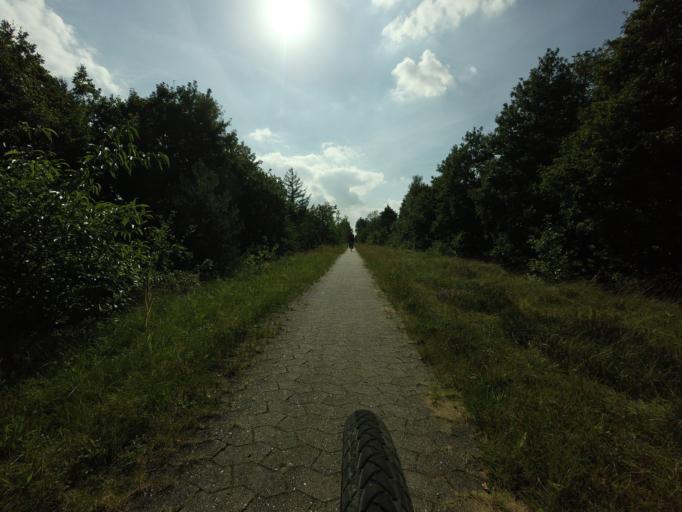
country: DK
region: Central Jutland
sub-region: Viborg Kommune
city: Karup
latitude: 56.2671
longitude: 9.1141
